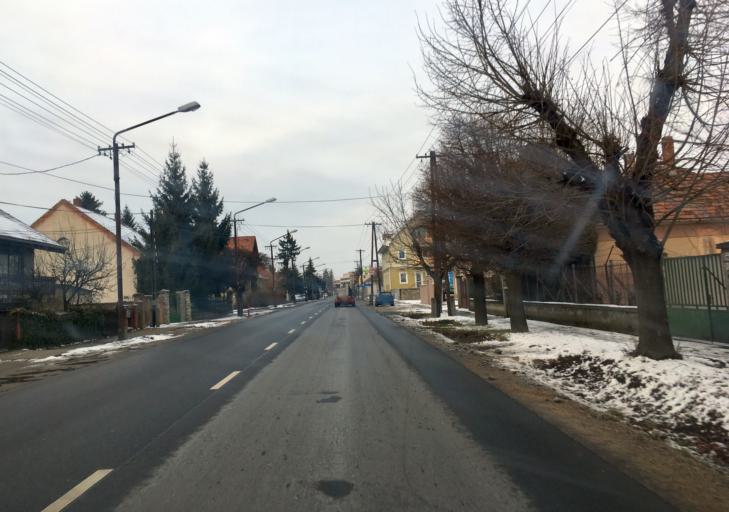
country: HU
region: Gyor-Moson-Sopron
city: Mosonmagyarovar
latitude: 47.8678
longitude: 17.2683
